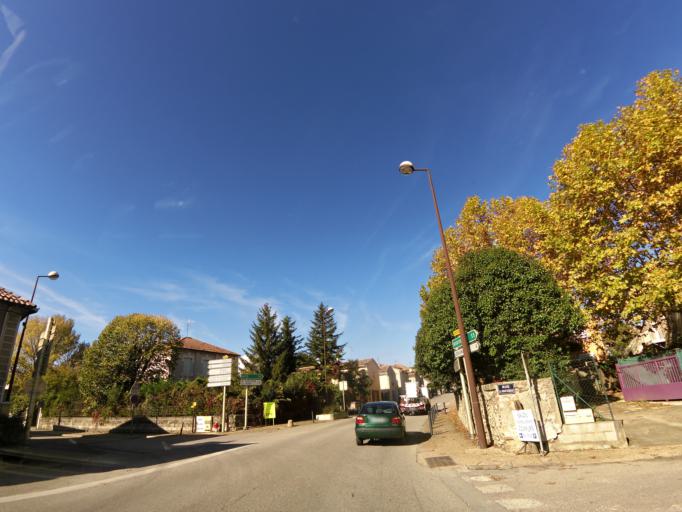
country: FR
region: Languedoc-Roussillon
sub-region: Departement du Gard
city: Ribaute-les-Tavernes
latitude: 44.0340
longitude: 4.1023
